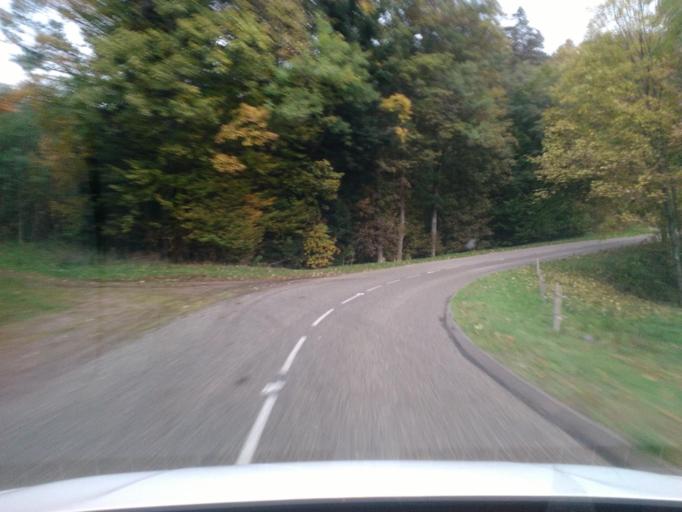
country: FR
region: Lorraine
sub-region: Departement des Vosges
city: Ban-de-Laveline
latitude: 48.3576
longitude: 7.1023
